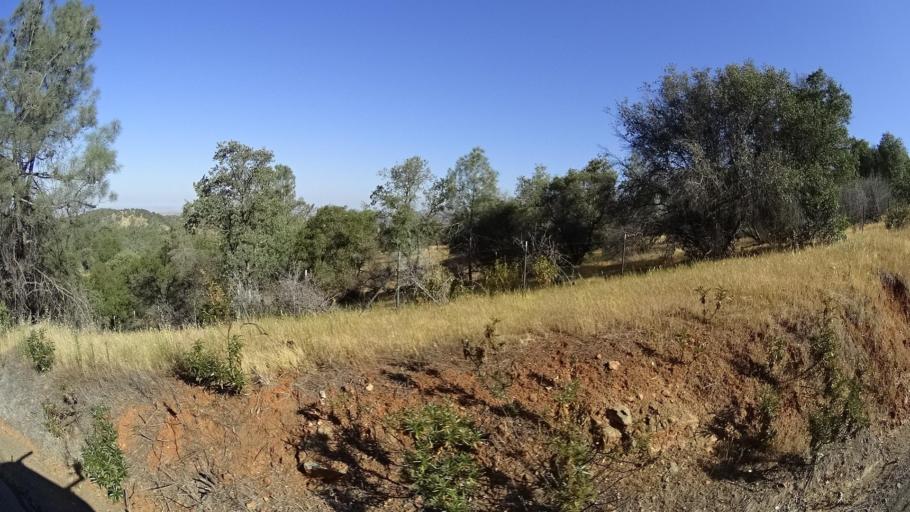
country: US
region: California
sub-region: Mariposa County
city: Mariposa
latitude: 37.5642
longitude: -120.1581
